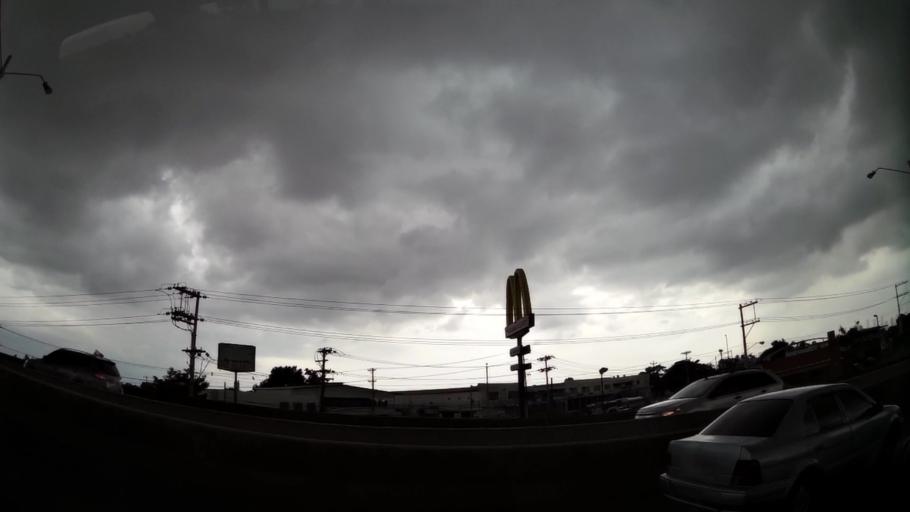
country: PA
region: Panama
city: San Miguelito
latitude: 9.0576
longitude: -79.4337
